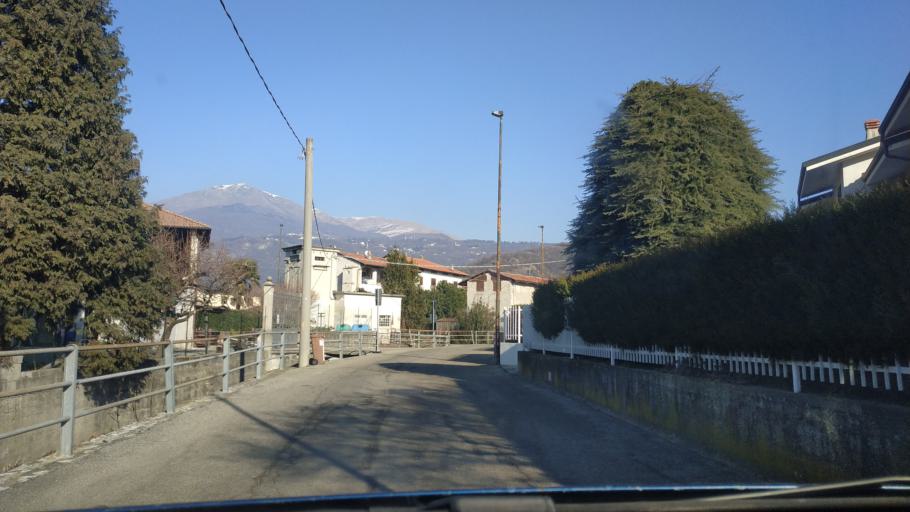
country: IT
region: Piedmont
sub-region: Provincia di Torino
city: Montalto Dora
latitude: 45.4922
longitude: 7.8590
